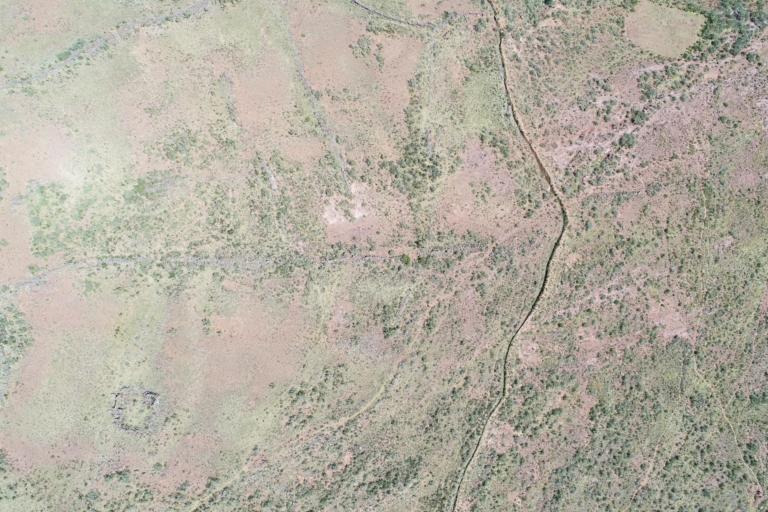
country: BO
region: La Paz
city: Tiahuanaco
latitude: -16.6078
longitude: -68.7588
